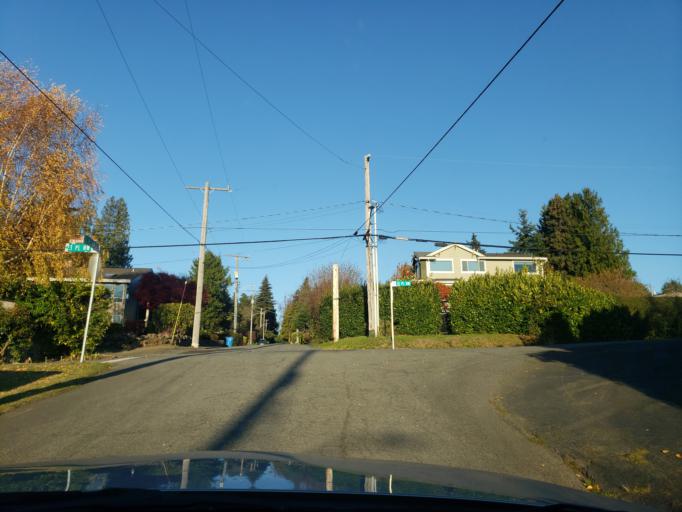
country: US
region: Washington
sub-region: Snohomish County
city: Woodway
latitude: 47.7760
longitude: -122.3857
